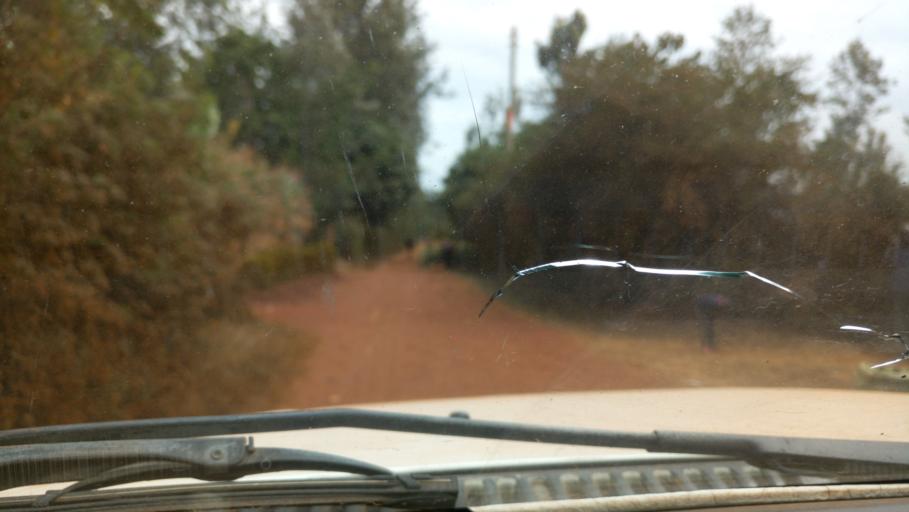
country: KE
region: Murang'a District
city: Maragua
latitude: -0.7727
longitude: 37.1477
